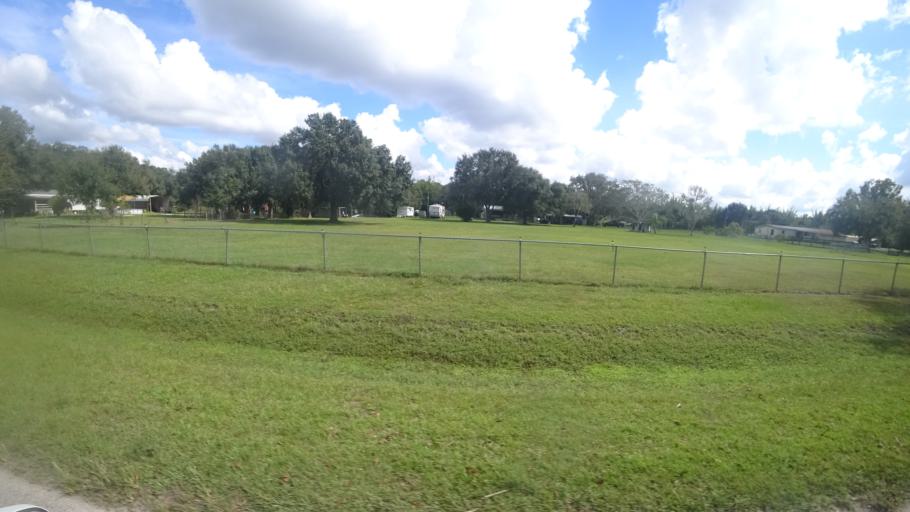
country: US
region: Florida
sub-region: Hillsborough County
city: Sun City Center
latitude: 27.6537
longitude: -82.3635
